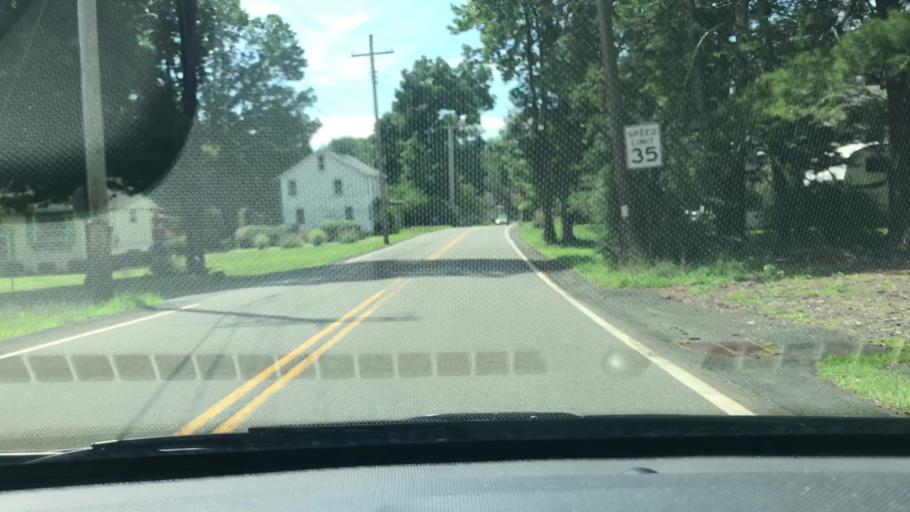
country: US
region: New York
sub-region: Ulster County
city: Shokan
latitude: 41.9298
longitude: -74.2160
